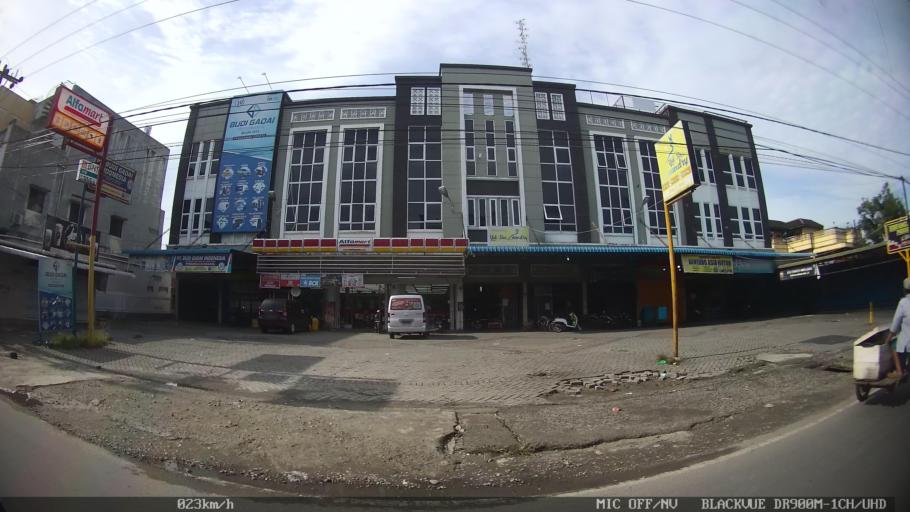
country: ID
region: North Sumatra
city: Medan
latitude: 3.6098
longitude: 98.6437
